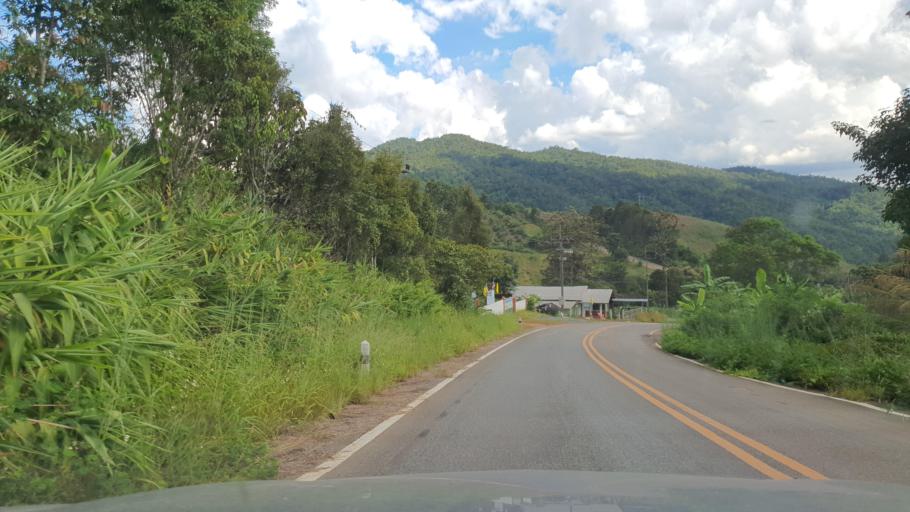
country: TH
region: Chiang Rai
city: Wiang Pa Pao
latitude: 19.3110
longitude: 99.4088
